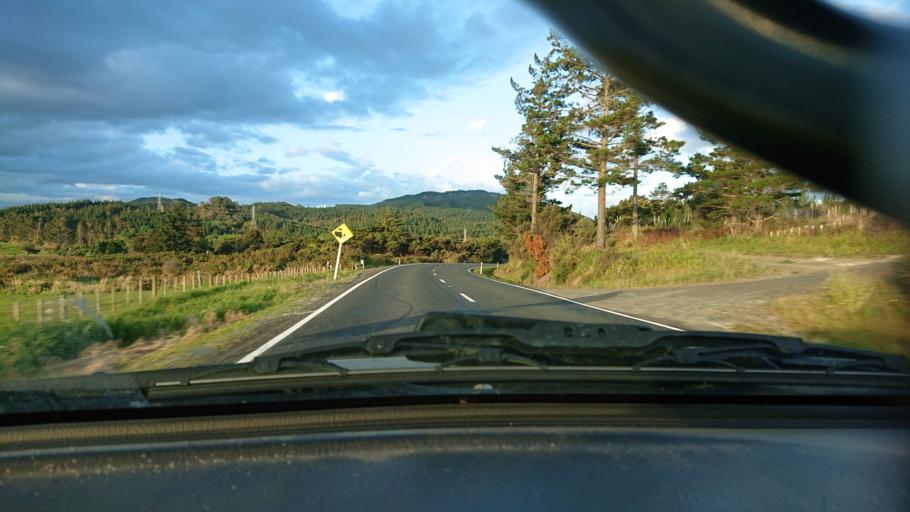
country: NZ
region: Auckland
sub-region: Auckland
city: Parakai
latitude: -36.5110
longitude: 174.4530
